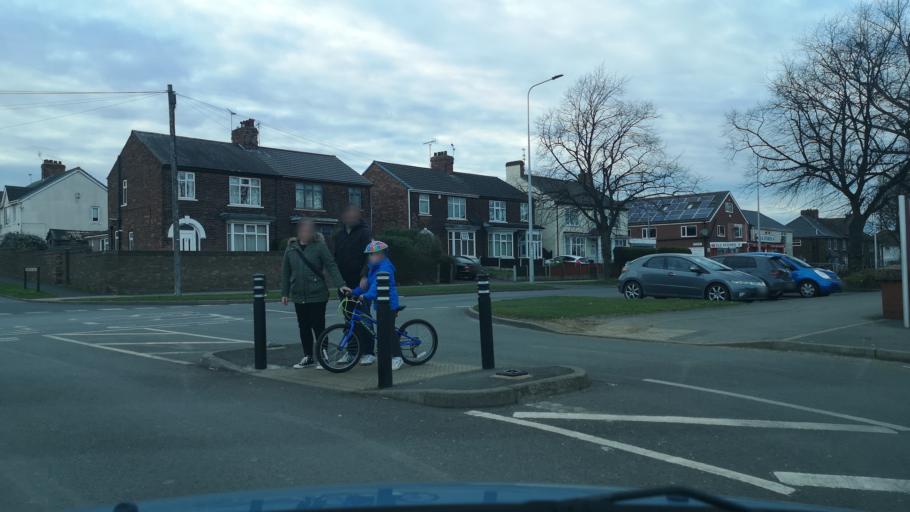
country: GB
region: England
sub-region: North Lincolnshire
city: Scunthorpe
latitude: 53.5914
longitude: -0.6609
